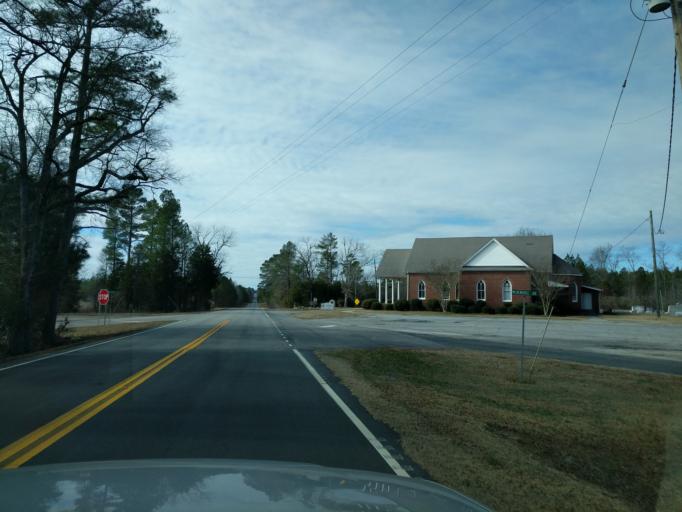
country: US
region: South Carolina
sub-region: Edgefield County
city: Edgefield
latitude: 33.9344
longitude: -81.9701
